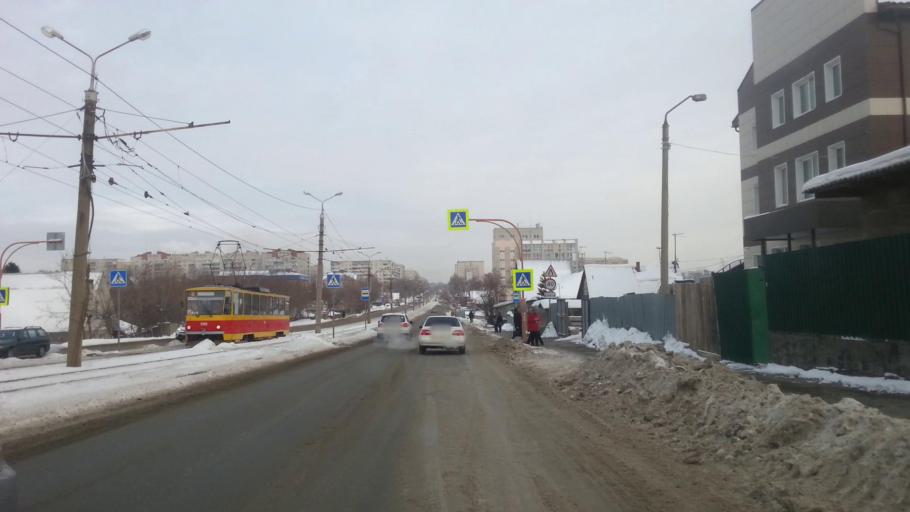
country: RU
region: Altai Krai
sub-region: Gorod Barnaulskiy
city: Barnaul
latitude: 53.3664
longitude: 83.7321
